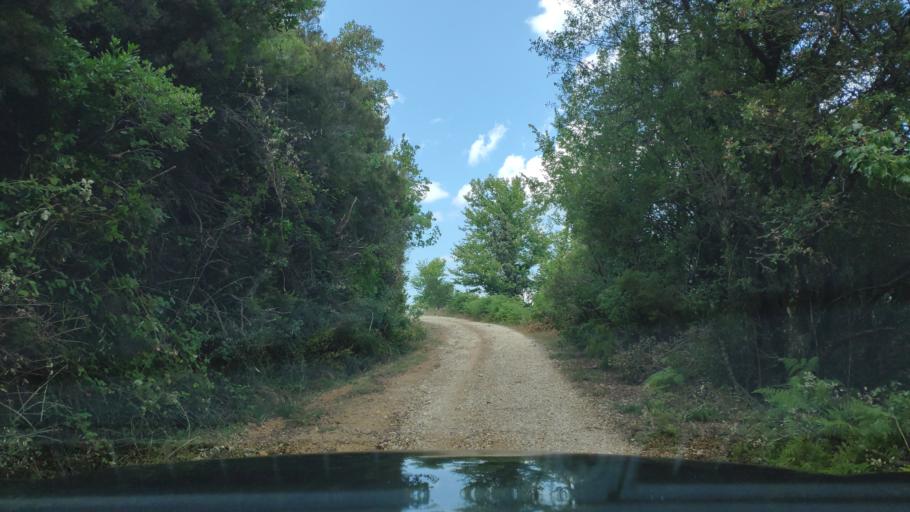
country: GR
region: Epirus
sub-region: Nomos Artas
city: Agios Dimitrios
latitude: 39.3099
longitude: 21.0223
